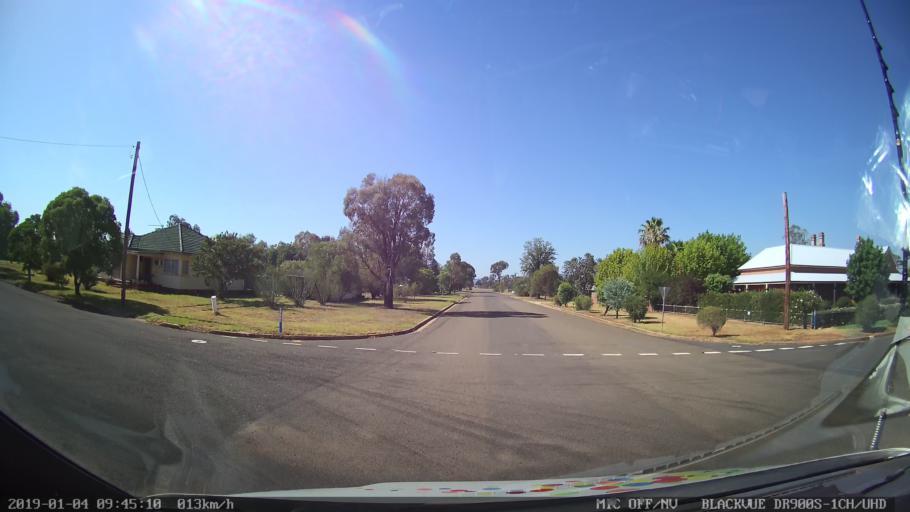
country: AU
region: New South Wales
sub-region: Cabonne
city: Canowindra
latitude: -33.6150
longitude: 148.4330
